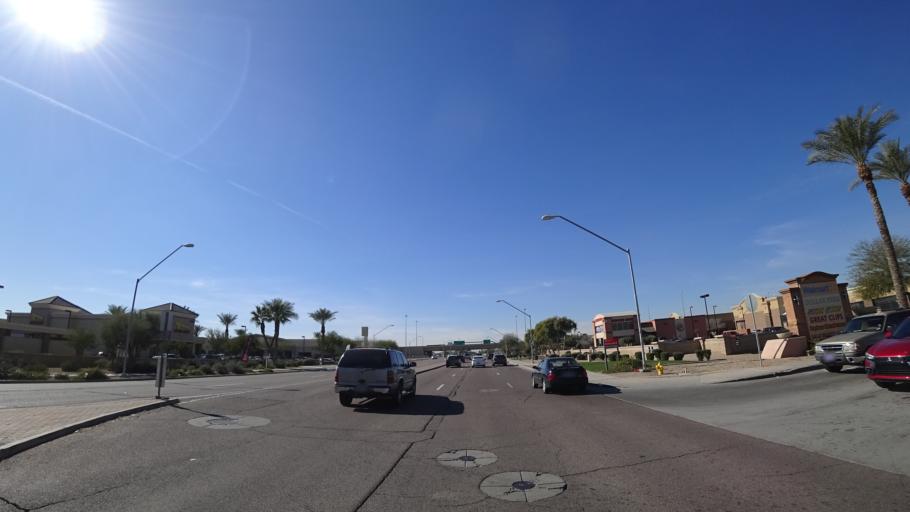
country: US
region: Arizona
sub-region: Maricopa County
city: Tolleson
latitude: 33.5086
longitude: -112.2660
